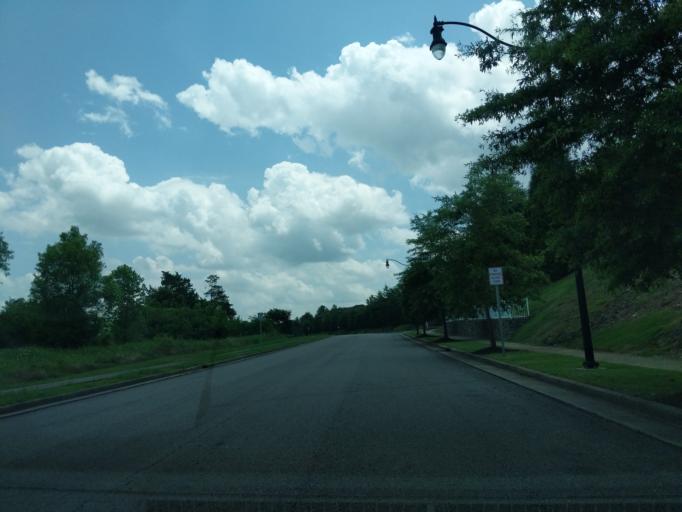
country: US
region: Tennessee
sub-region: Davidson County
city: Goodlettsville
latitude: 36.2985
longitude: -86.7277
